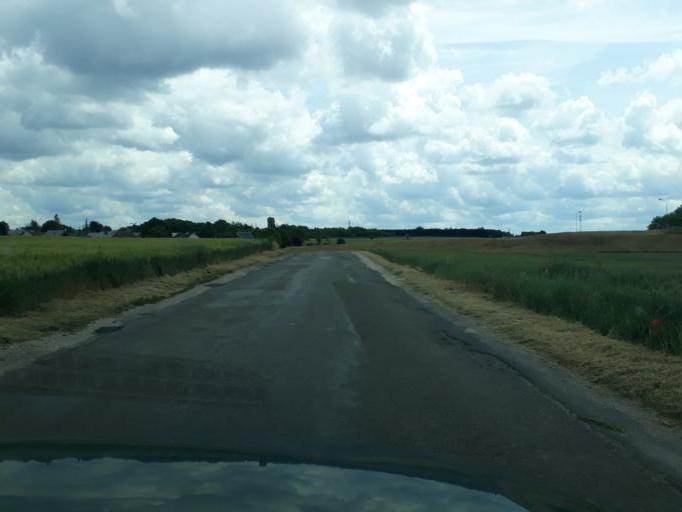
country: FR
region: Centre
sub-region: Departement du Loiret
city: Ingre
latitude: 47.9125
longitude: 1.8196
